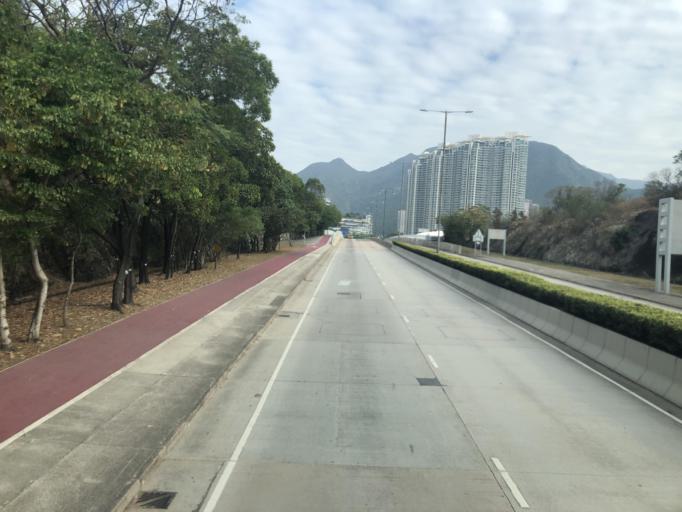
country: HK
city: Tai O
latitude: 22.2914
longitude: 113.9328
